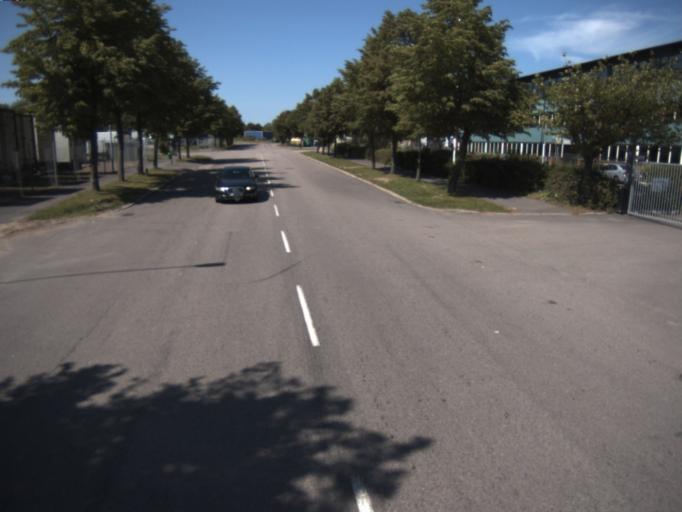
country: SE
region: Skane
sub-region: Helsingborg
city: Gantofta
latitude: 56.0088
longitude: 12.7675
